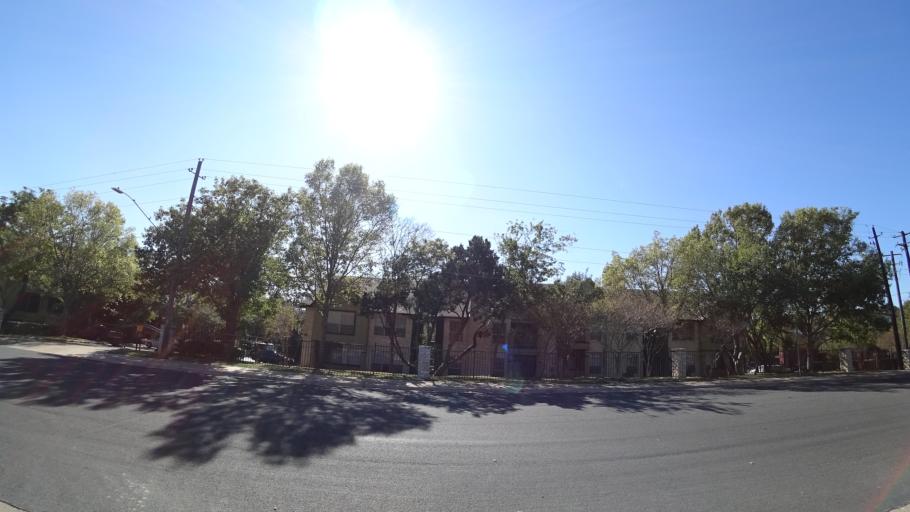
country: US
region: Texas
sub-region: Williamson County
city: Jollyville
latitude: 30.4111
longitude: -97.7531
